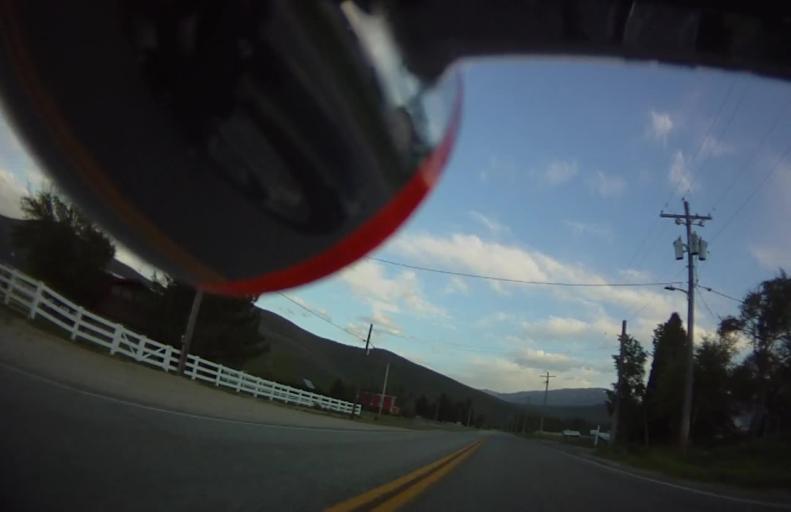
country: US
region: Utah
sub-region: Wasatch County
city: Midway
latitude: 40.4669
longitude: -111.4717
